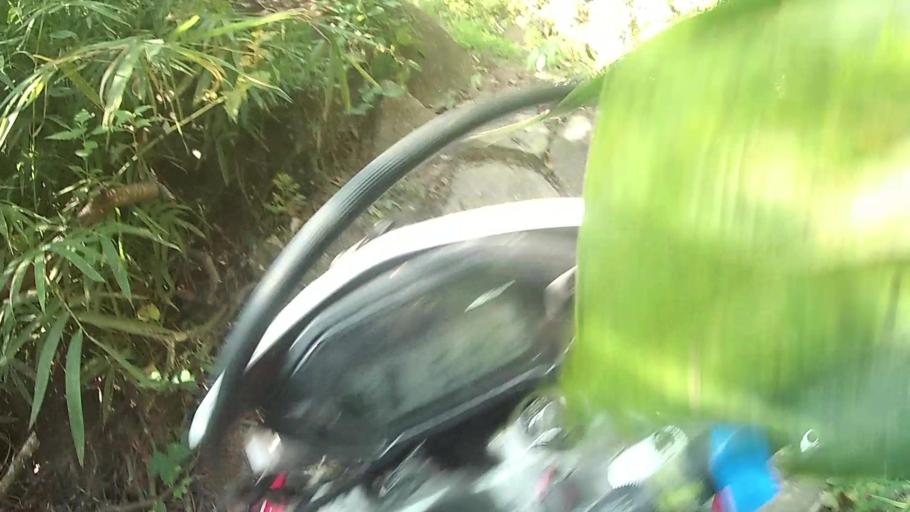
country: TH
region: Chiang Mai
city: Phrao
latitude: 19.4111
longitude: 99.2975
